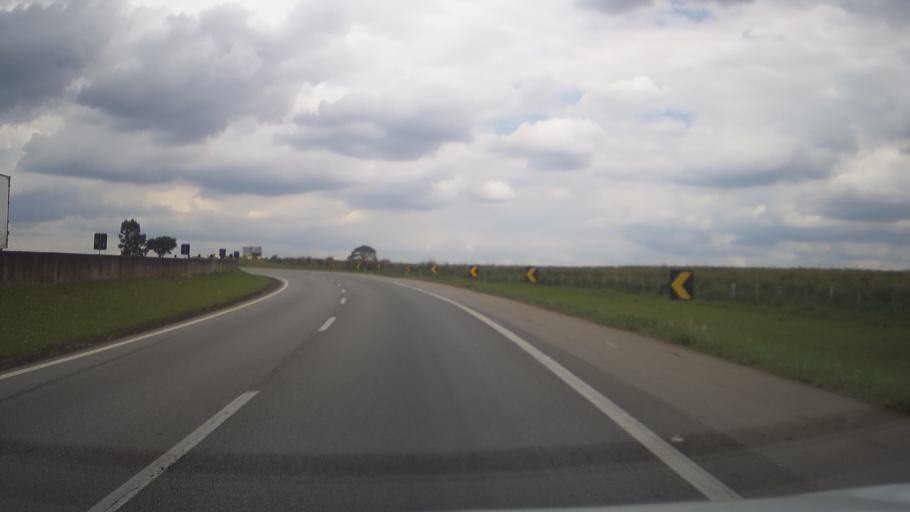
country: BR
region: Minas Gerais
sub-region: Tres Coracoes
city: Tres Coracoes
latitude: -21.4896
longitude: -45.2079
